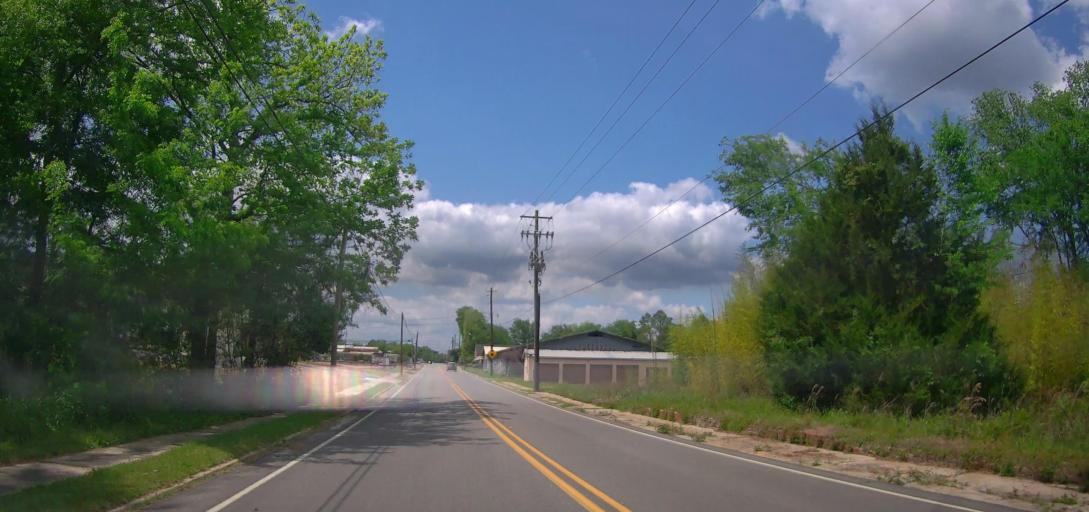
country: US
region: Georgia
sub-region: Treutlen County
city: Soperton
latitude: 32.3769
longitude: -82.5885
